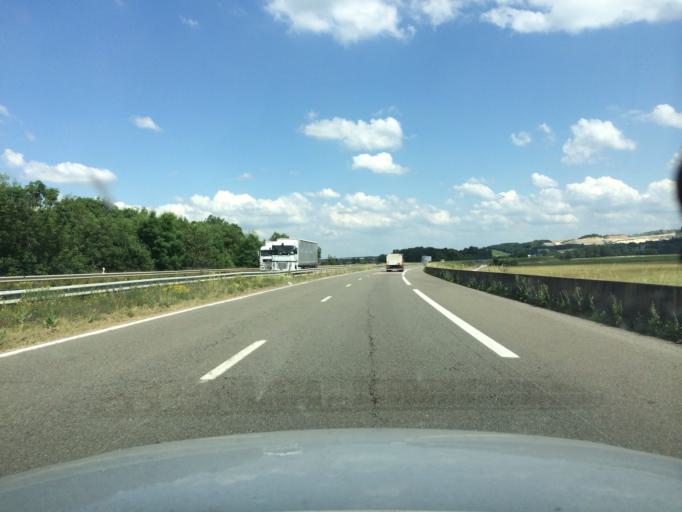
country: FR
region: Lorraine
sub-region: Departement de Meurthe-et-Moselle
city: Foug
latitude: 48.6896
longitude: 5.7013
